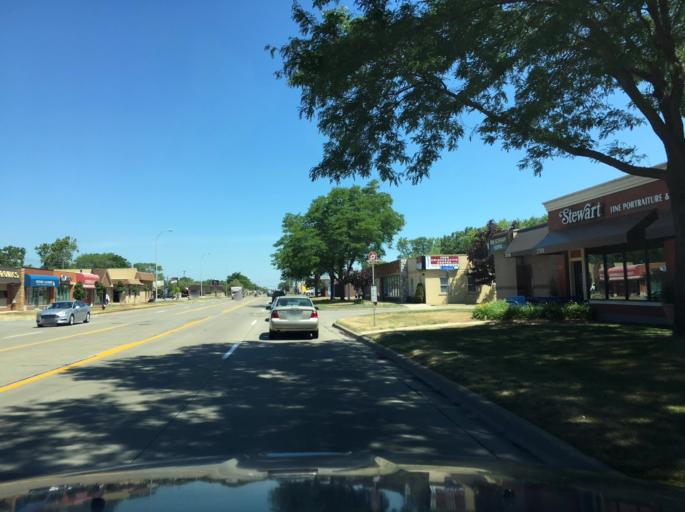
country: US
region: Michigan
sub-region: Macomb County
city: Saint Clair Shores
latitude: 42.4909
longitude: -82.8971
